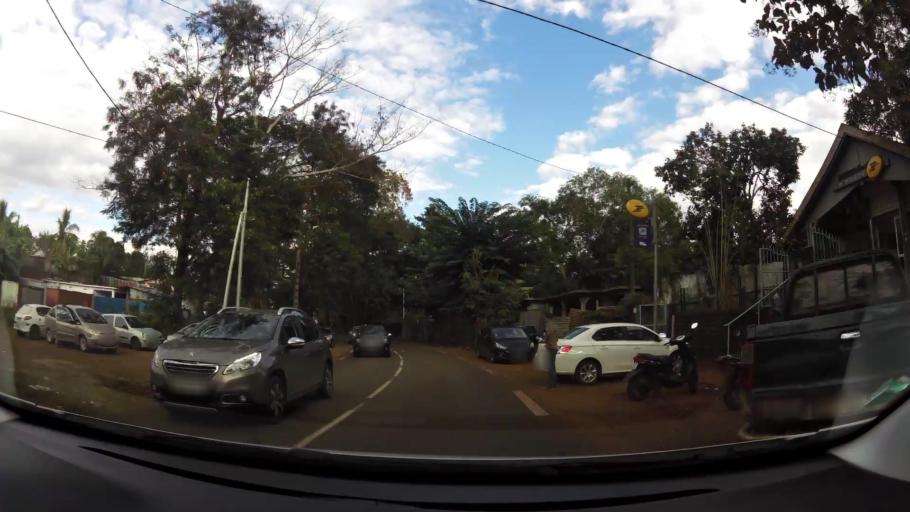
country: YT
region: Ouangani
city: Ouangani
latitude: -12.8338
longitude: 45.1326
